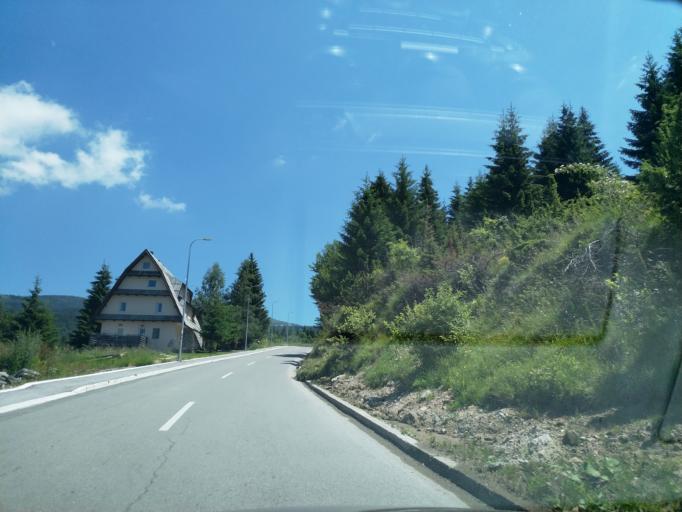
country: RS
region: Central Serbia
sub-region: Raski Okrug
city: Raska
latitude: 43.2735
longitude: 20.7702
